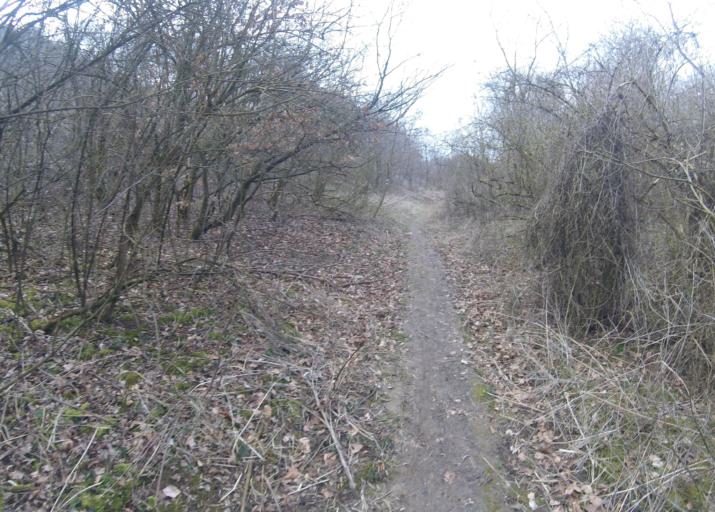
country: HU
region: Heves
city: Belapatfalva
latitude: 48.0473
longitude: 20.3660
